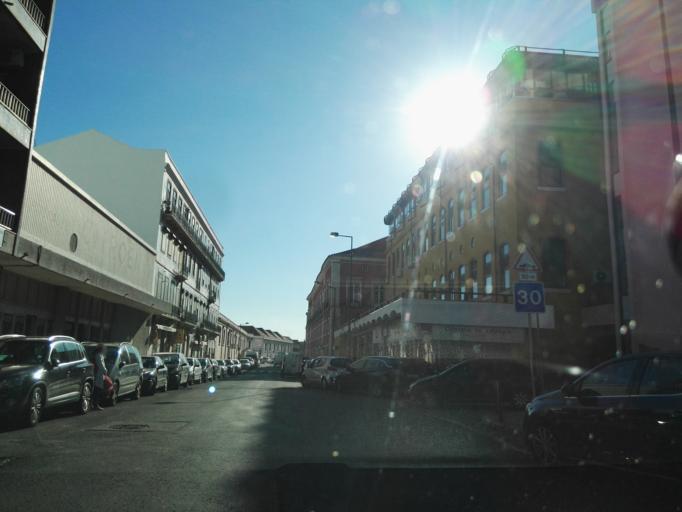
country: PT
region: Lisbon
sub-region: Lisbon
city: Lisbon
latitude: 38.7283
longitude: -9.1096
